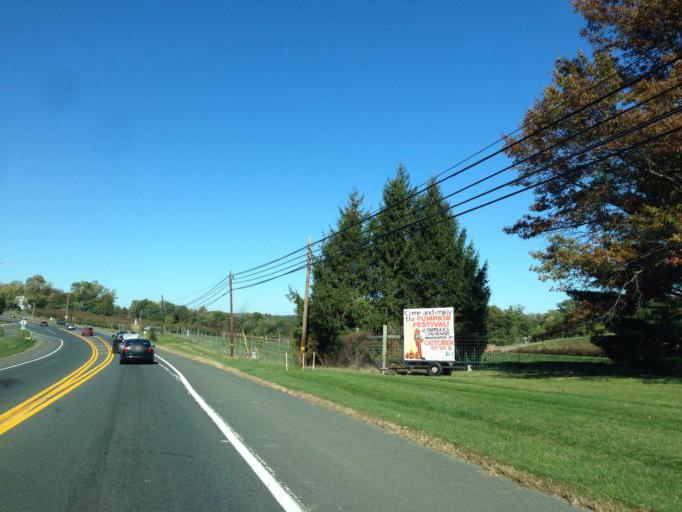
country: US
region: Maryland
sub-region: Montgomery County
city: Clarksburg
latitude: 39.2230
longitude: -77.2373
